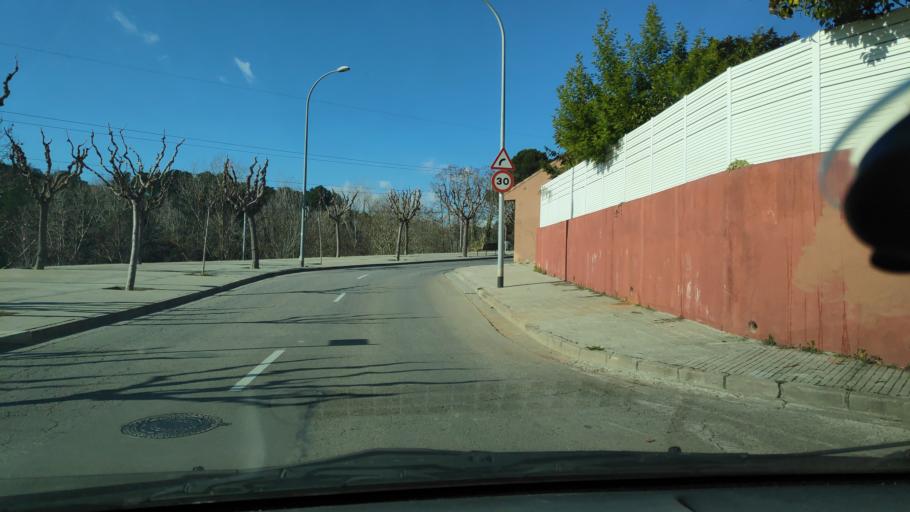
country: ES
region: Catalonia
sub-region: Provincia de Barcelona
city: Sant Quirze del Valles
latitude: 41.5328
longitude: 2.0726
